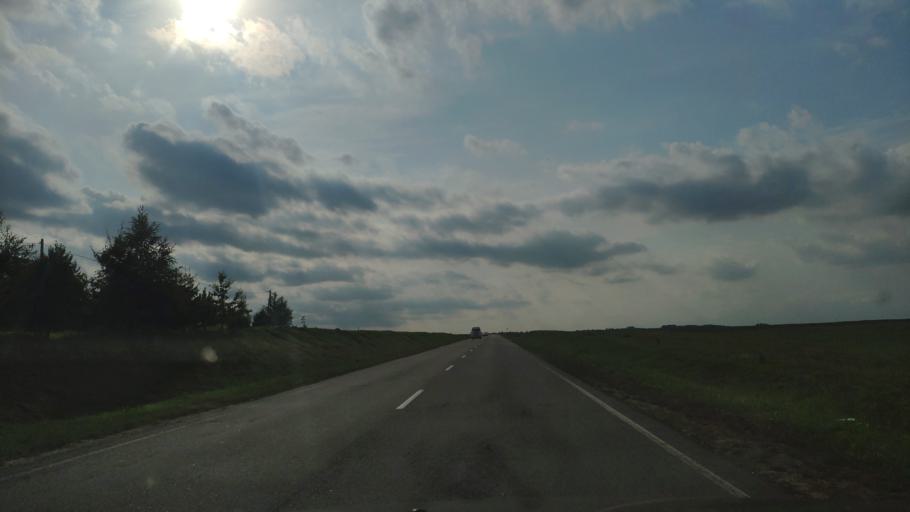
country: BY
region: Minsk
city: Azyartso
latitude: 53.8354
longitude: 27.3456
